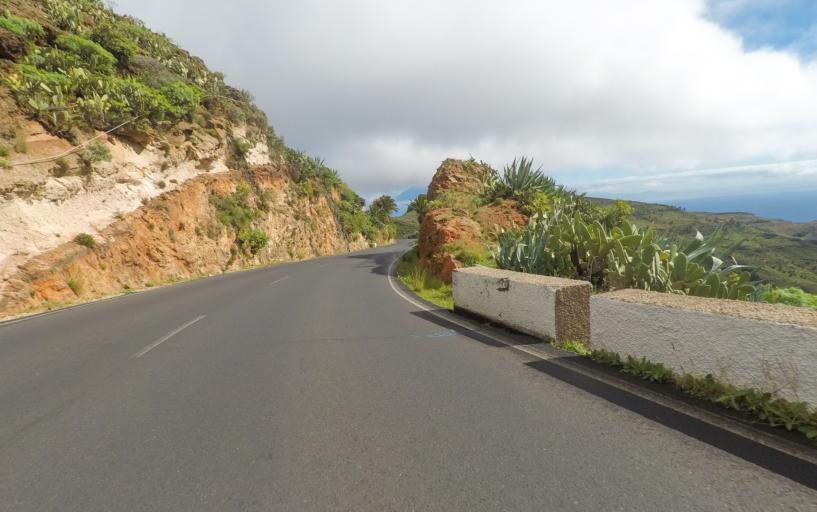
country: ES
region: Canary Islands
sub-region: Provincia de Santa Cruz de Tenerife
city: San Sebastian de la Gomera
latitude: 28.0989
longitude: -17.1734
